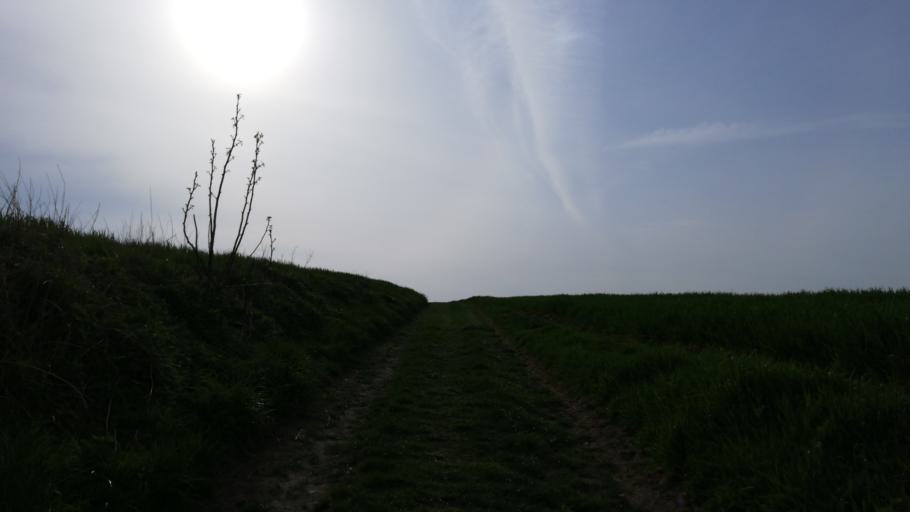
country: AT
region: Upper Austria
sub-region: Politischer Bezirk Grieskirchen
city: Bad Schallerbach
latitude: 48.1897
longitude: 13.9495
